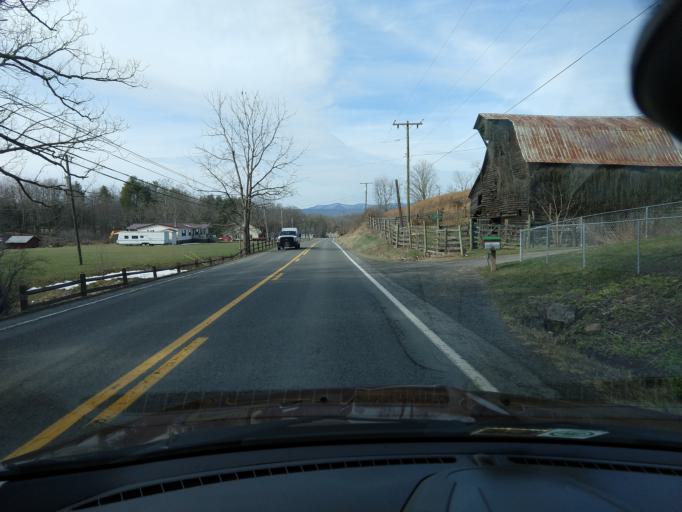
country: US
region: West Virginia
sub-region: Pocahontas County
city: Marlinton
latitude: 38.1652
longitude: -80.1608
